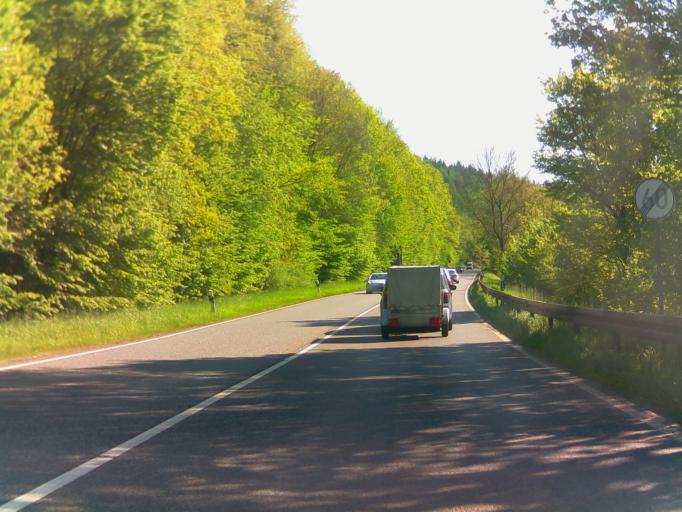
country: DE
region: Hesse
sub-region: Regierungsbezirk Darmstadt
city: Wachtersbach
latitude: 50.2519
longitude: 9.3016
